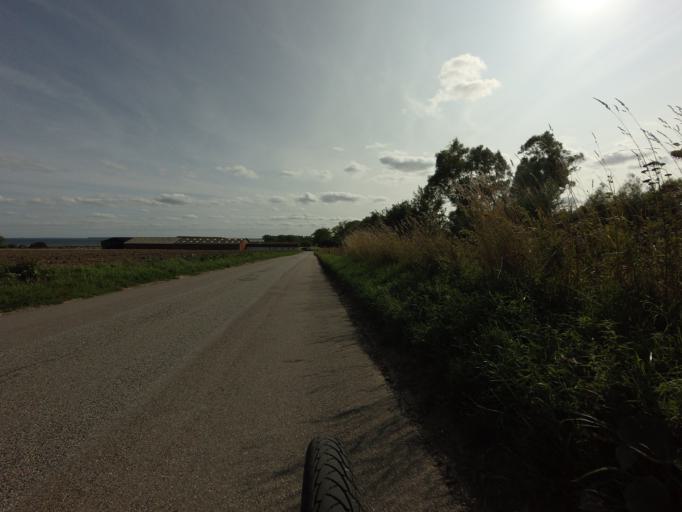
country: DK
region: Zealand
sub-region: Faxe Kommune
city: Fakse
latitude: 55.1887
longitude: 12.1133
